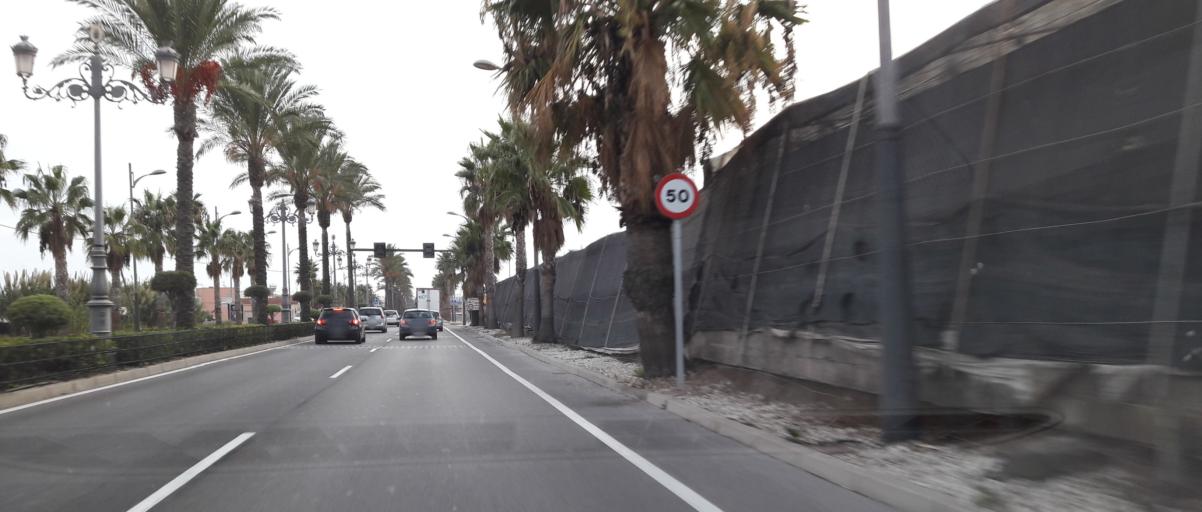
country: ES
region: Andalusia
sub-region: Provincia de Almeria
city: Roquetas de Mar
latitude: 36.7956
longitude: -2.6031
